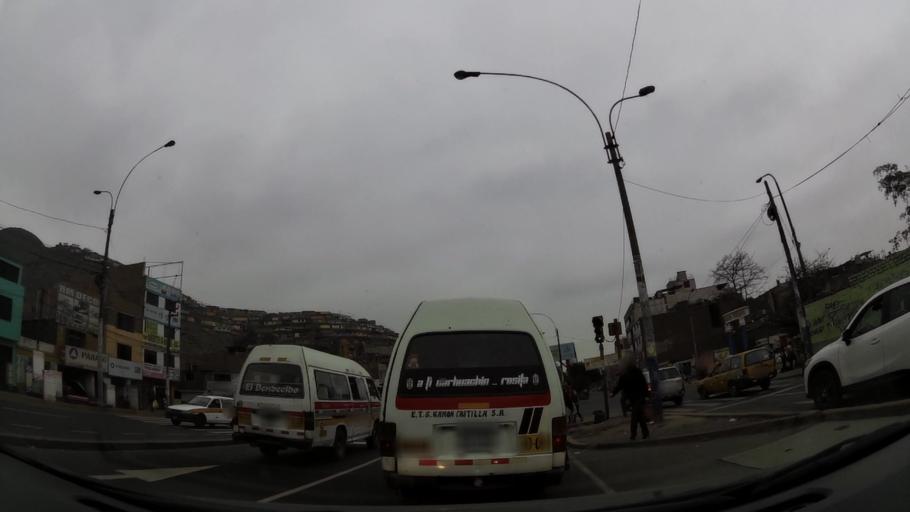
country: PE
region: Lima
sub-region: Lima
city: Independencia
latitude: -11.9658
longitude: -77.0558
